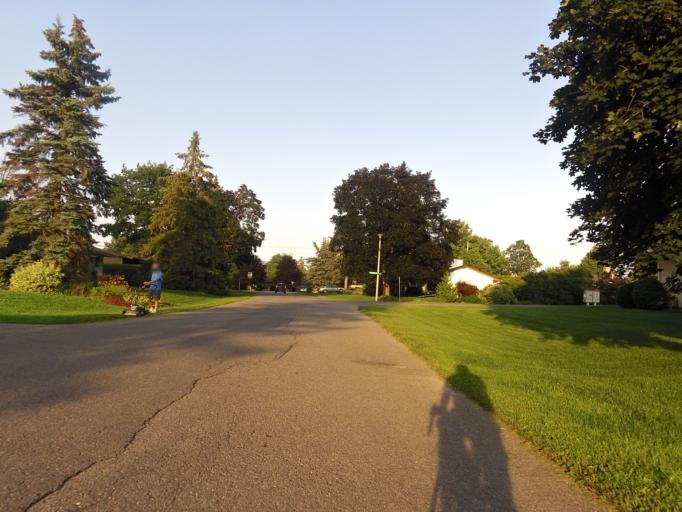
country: CA
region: Ontario
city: Bells Corners
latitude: 45.3184
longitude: -75.8201
